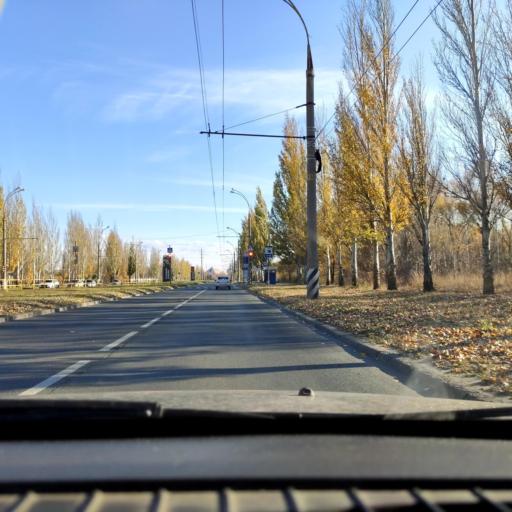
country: RU
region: Samara
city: Tol'yatti
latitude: 53.5481
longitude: 49.2730
